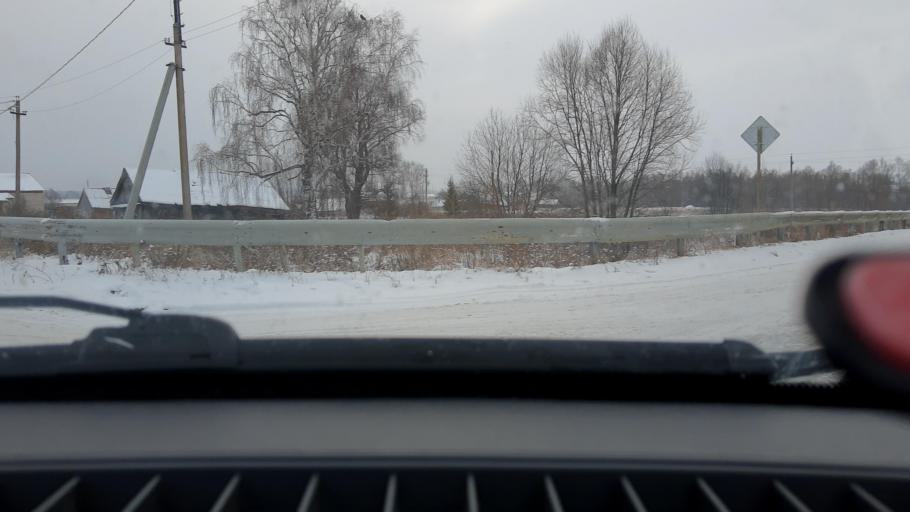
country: RU
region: Bashkortostan
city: Iglino
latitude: 54.6438
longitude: 56.4246
